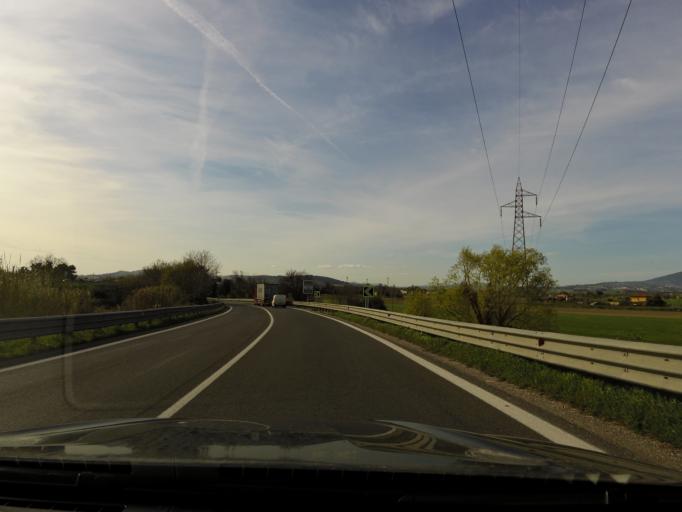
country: IT
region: The Marches
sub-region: Provincia di Ancona
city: Loreto Stazione
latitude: 43.4443
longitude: 13.6337
